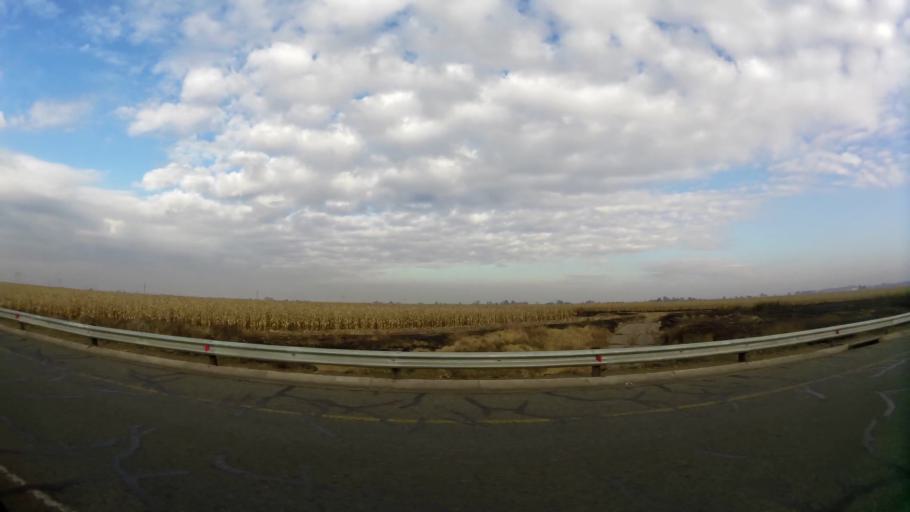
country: ZA
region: Gauteng
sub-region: Sedibeng District Municipality
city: Vanderbijlpark
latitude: -26.6600
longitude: 27.7846
